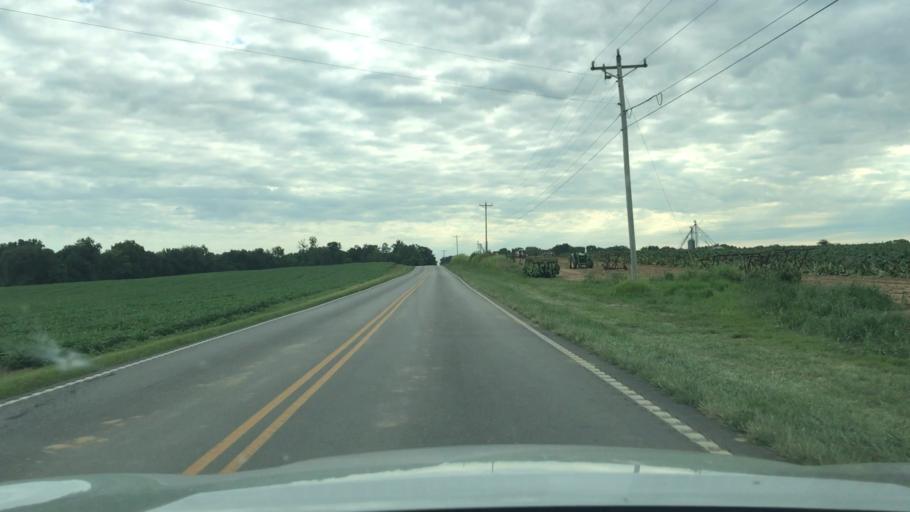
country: US
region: Kentucky
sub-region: Todd County
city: Elkton
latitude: 36.7450
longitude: -87.1771
